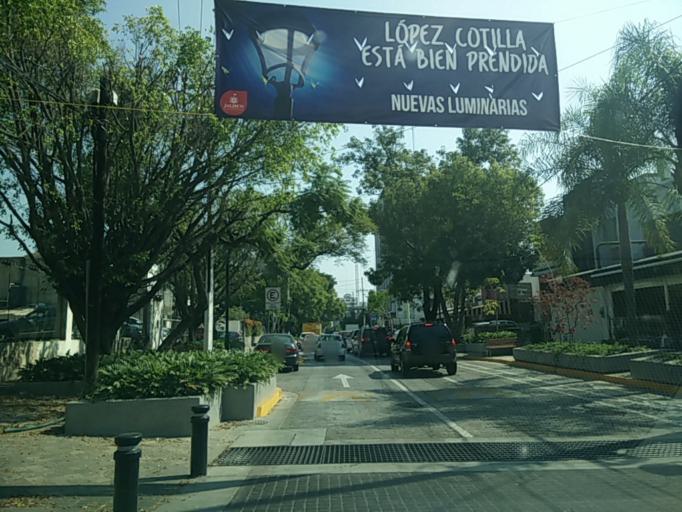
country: MX
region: Jalisco
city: Guadalajara
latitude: 20.6736
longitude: -103.3748
